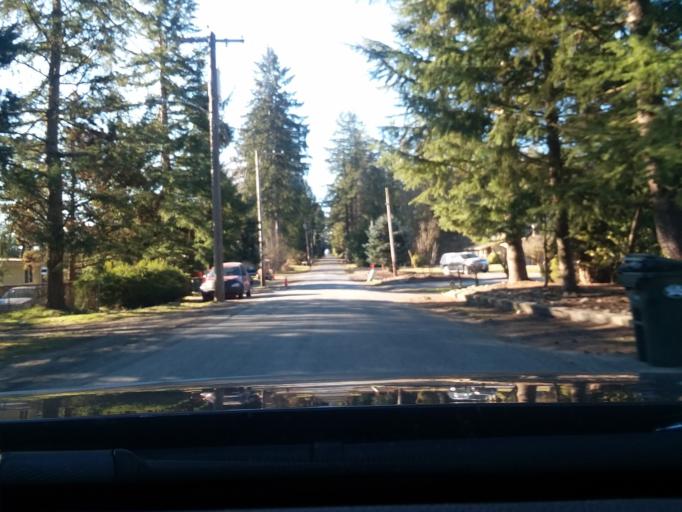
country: US
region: Washington
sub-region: Pierce County
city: Summit
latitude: 47.1373
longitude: -122.3628
